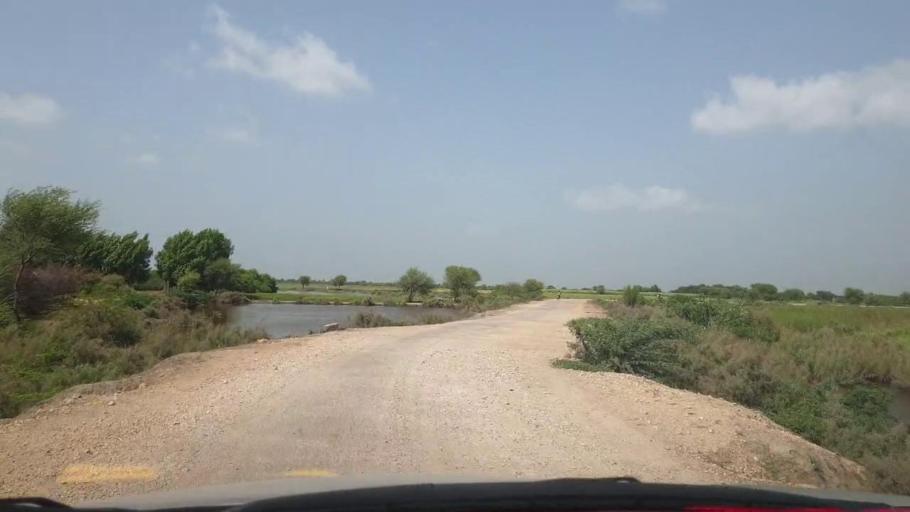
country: PK
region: Sindh
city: Tando Bago
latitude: 24.8715
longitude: 68.9273
